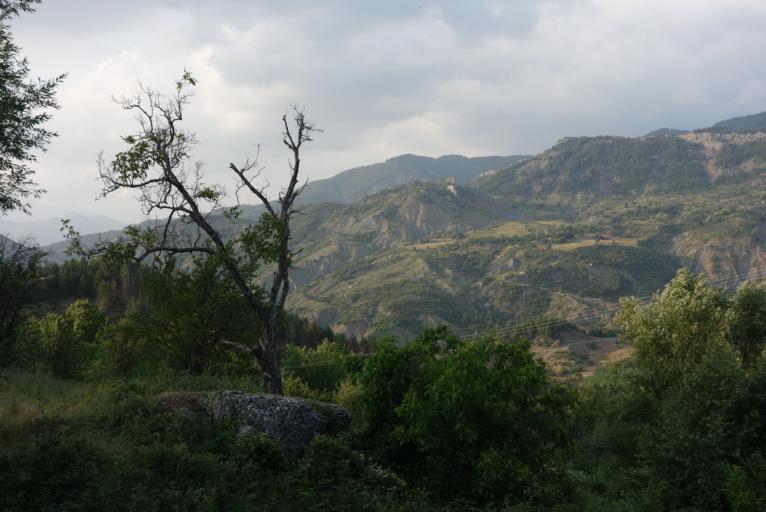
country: AL
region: Gjirokaster
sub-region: Rrethi i Permetit
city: Frasher
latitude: 40.3609
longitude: 20.4285
